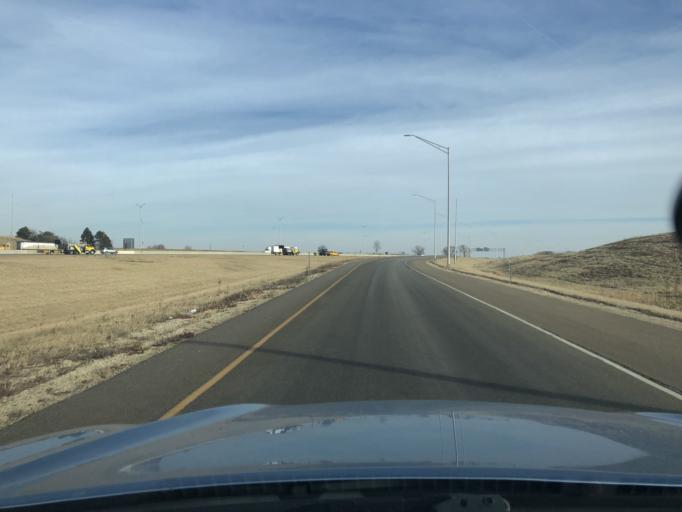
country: US
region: Illinois
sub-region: Boone County
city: Belvidere
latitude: 42.2325
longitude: -88.8135
